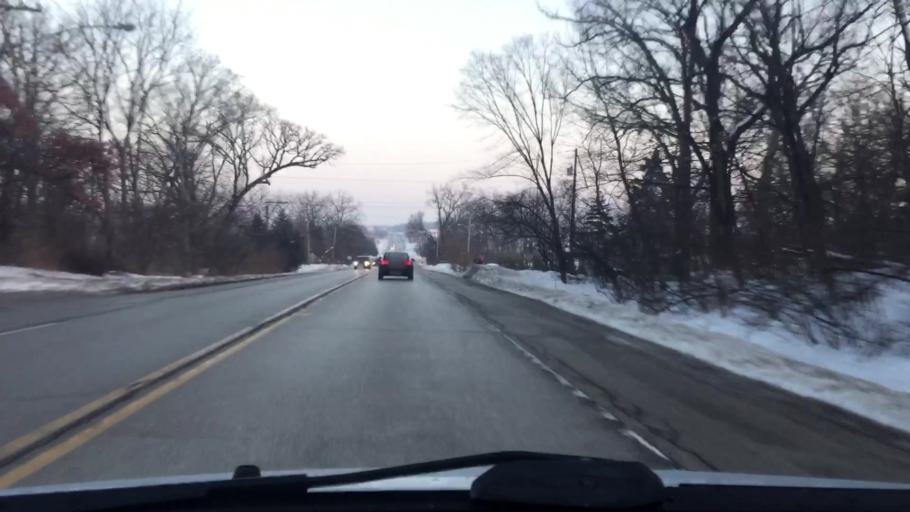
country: US
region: Illinois
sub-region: Kane County
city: Village of Campton Hills
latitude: 41.9232
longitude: -88.3672
